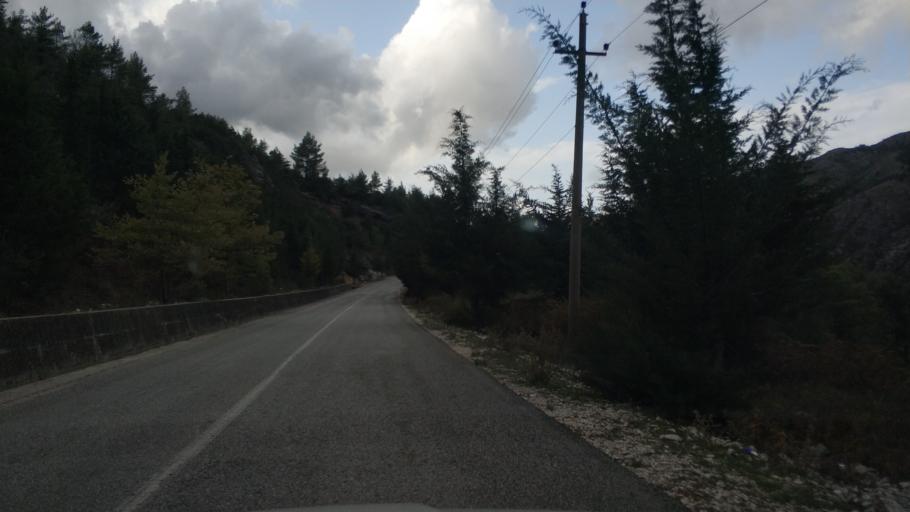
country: AL
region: Vlore
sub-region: Rrethi i Vlores
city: Orikum
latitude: 40.2491
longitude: 19.5435
